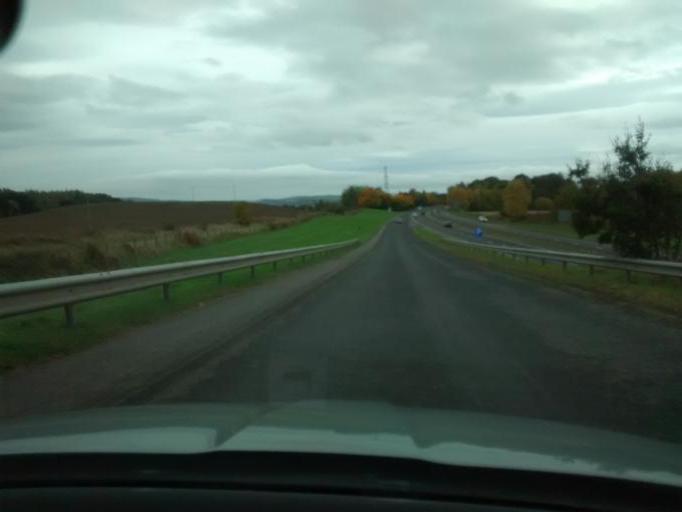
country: GB
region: Scotland
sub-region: Perth and Kinross
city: Luncarty
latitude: 56.4468
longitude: -3.4717
